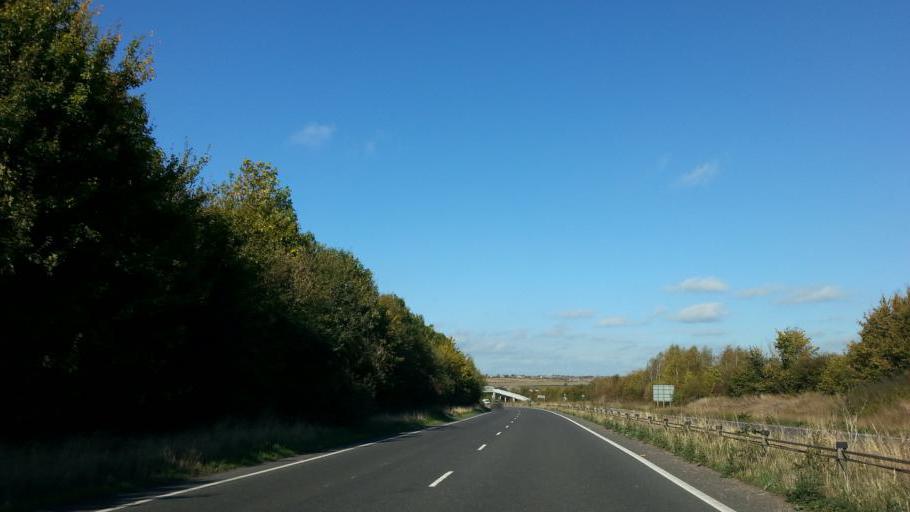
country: GB
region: England
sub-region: Northamptonshire
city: Higham Ferrers
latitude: 52.3151
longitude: -0.5878
